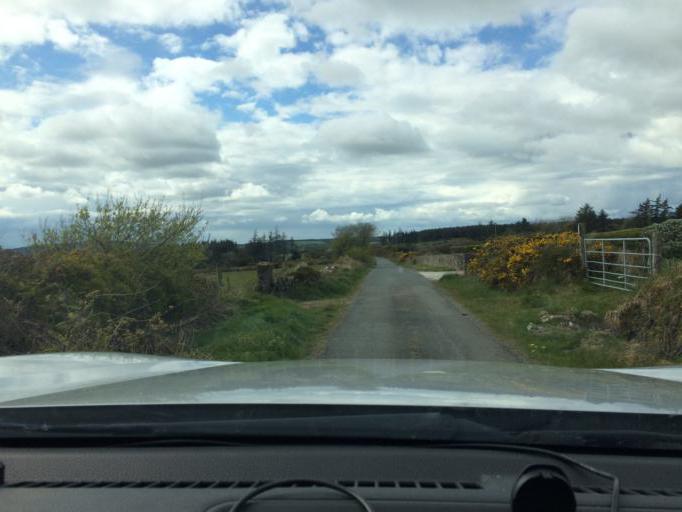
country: IE
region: Munster
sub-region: Waterford
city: Dungarvan
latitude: 52.0402
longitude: -7.6321
